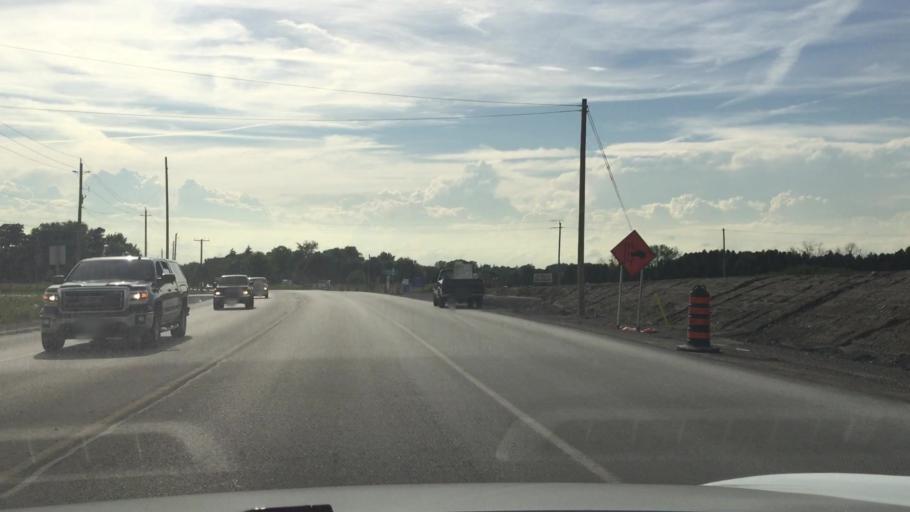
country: CA
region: Ontario
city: Oshawa
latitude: 43.9138
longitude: -78.7695
